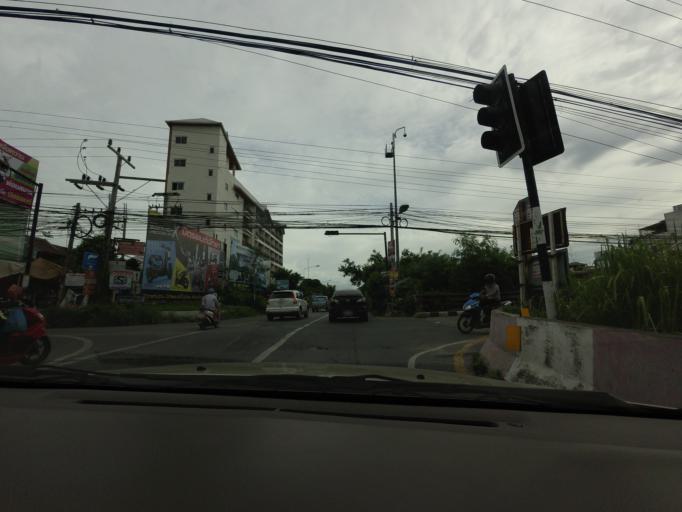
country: TH
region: Chon Buri
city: Phatthaya
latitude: 12.9320
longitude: 100.9057
